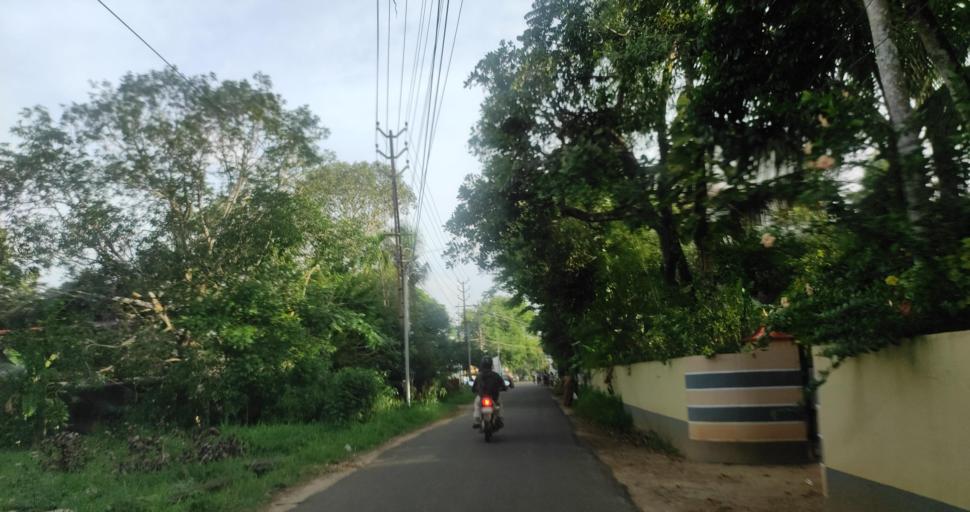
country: IN
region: Kerala
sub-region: Alappuzha
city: Shertallai
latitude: 9.6395
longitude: 76.3439
